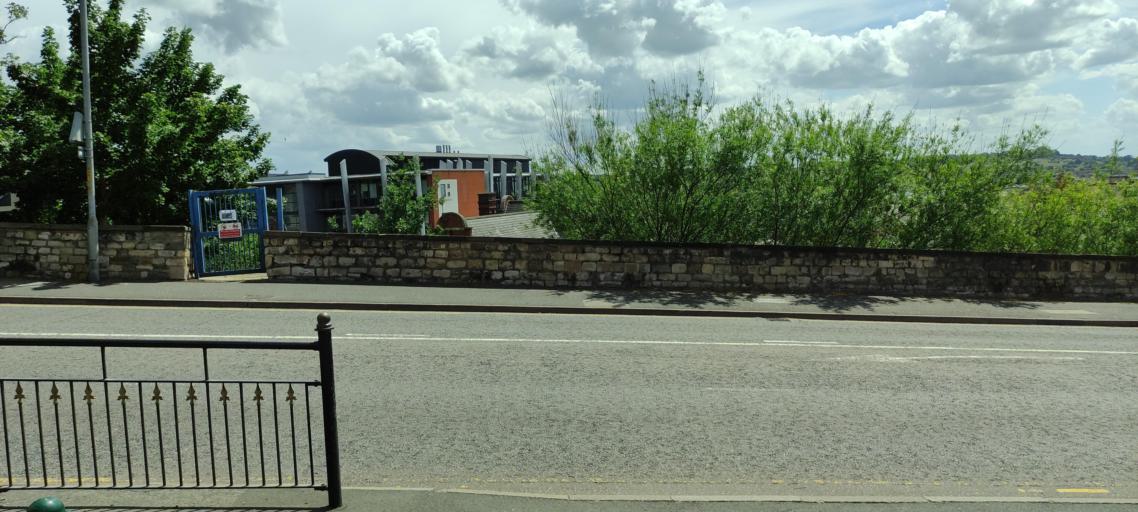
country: GB
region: England
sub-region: Lincolnshire
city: Lincoln
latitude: 53.2322
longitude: -0.5344
